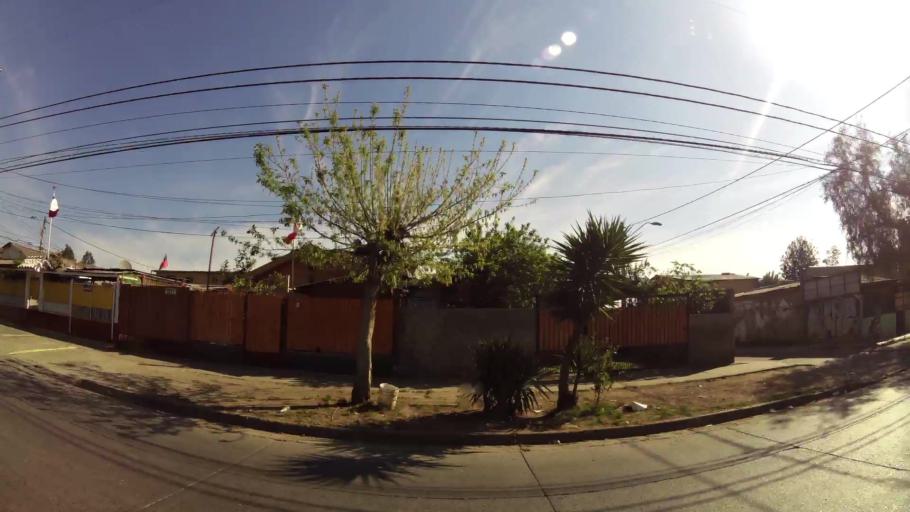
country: CL
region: Santiago Metropolitan
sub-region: Provincia de Santiago
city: Villa Presidente Frei, Nunoa, Santiago, Chile
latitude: -33.4741
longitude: -70.5668
